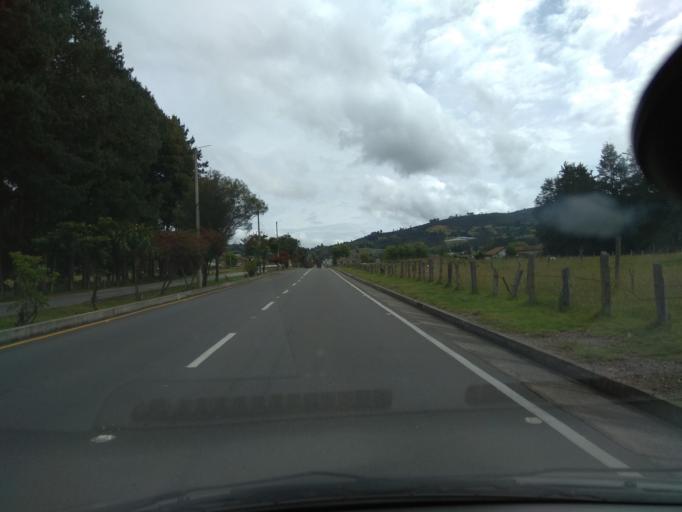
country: CO
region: Boyaca
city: Santa Rosa de Viterbo
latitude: 5.8719
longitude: -72.9879
